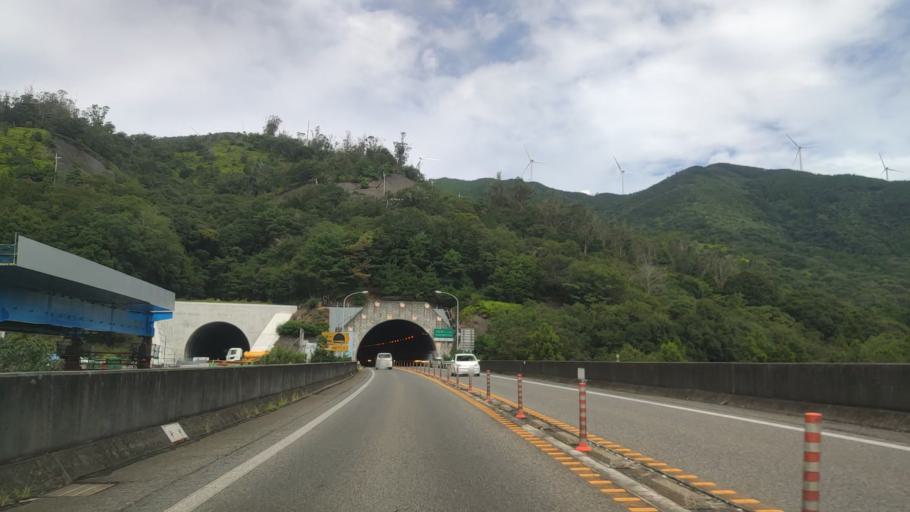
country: JP
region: Wakayama
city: Gobo
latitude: 33.9425
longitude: 135.1986
